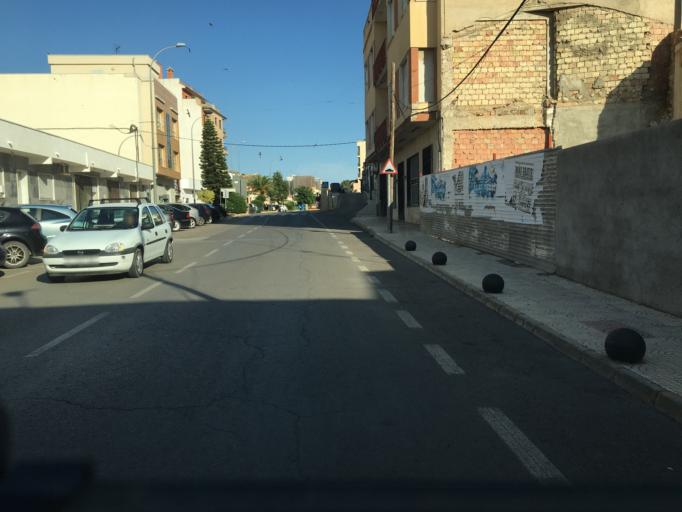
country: ES
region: Murcia
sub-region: Murcia
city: Puerto Lumbreras
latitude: 37.5622
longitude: -1.8104
